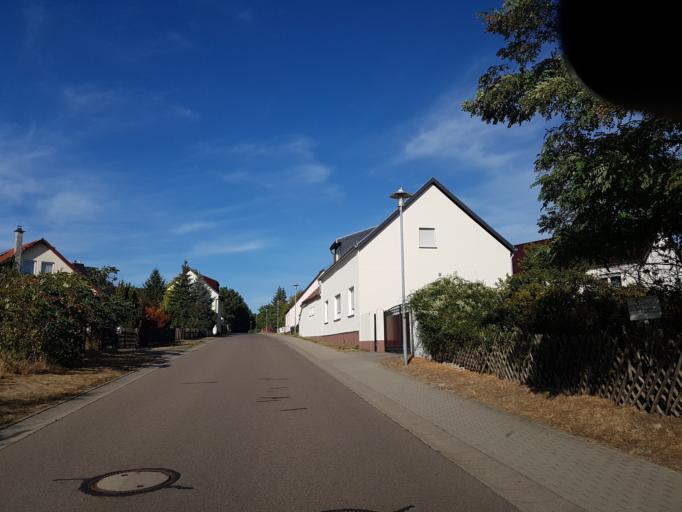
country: DE
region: Saxony-Anhalt
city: Jessen
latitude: 51.8029
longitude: 12.9728
